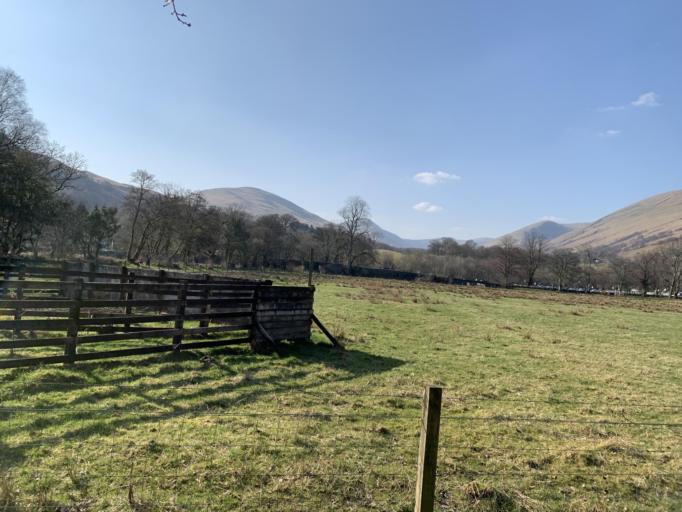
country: GB
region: Scotland
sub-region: West Dunbartonshire
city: Balloch
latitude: 56.0973
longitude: -4.6382
